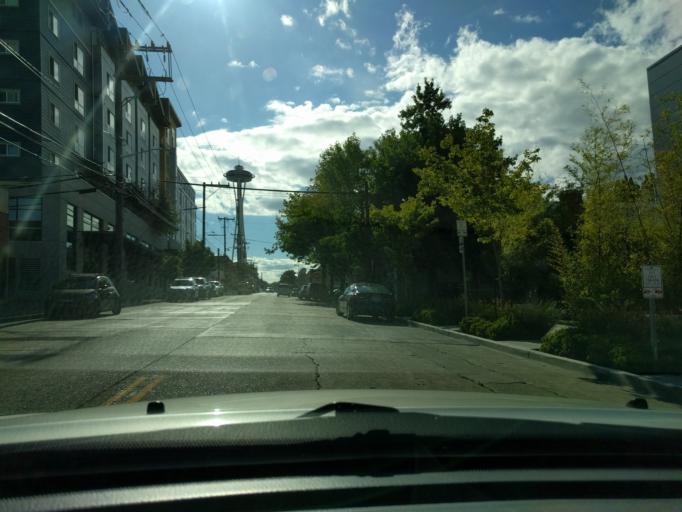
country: US
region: Washington
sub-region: King County
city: Seattle
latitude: 47.6209
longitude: -122.3401
